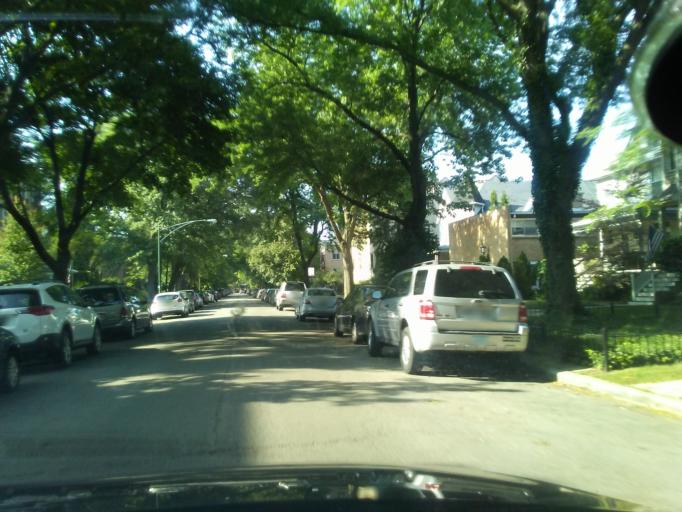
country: US
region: Illinois
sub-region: Cook County
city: Lincolnwood
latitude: 41.9701
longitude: -87.6727
